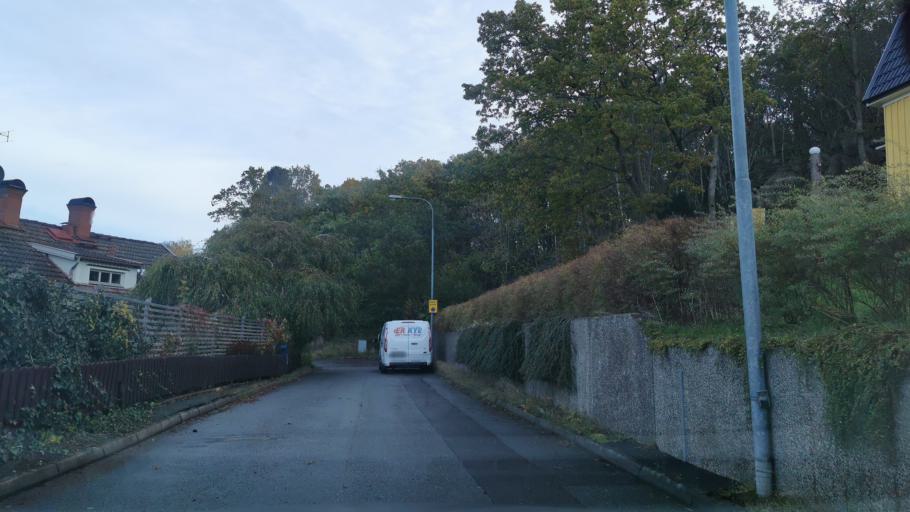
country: SE
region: Vaestra Goetaland
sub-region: Partille Kommun
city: Partille
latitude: 57.7324
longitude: 12.0841
